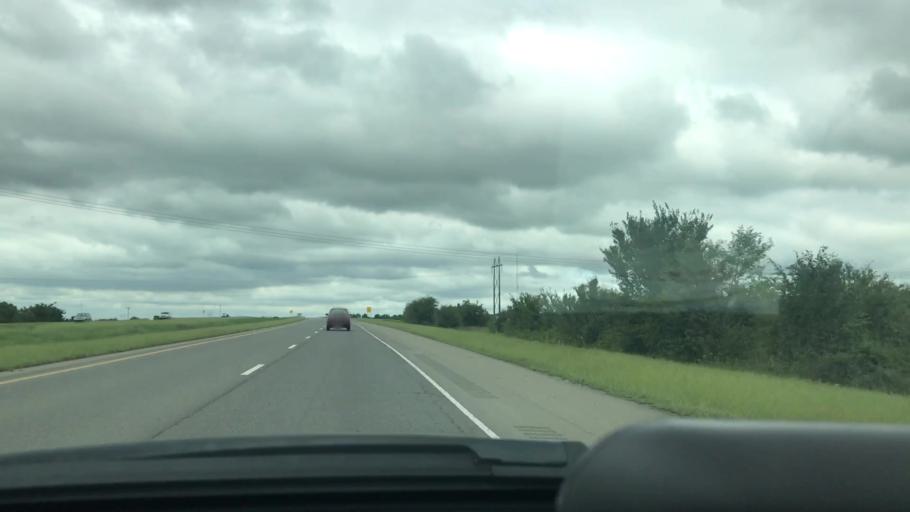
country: US
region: Oklahoma
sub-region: McIntosh County
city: Checotah
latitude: 35.5704
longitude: -95.4910
